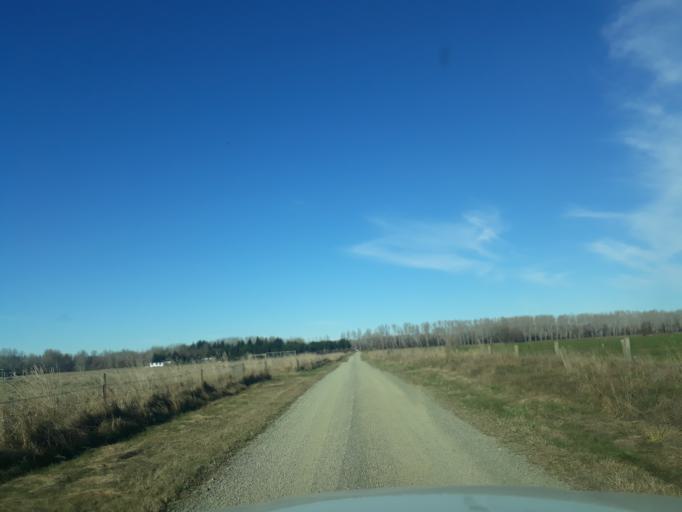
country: NZ
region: Canterbury
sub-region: Timaru District
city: Pleasant Point
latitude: -44.2541
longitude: 171.2189
